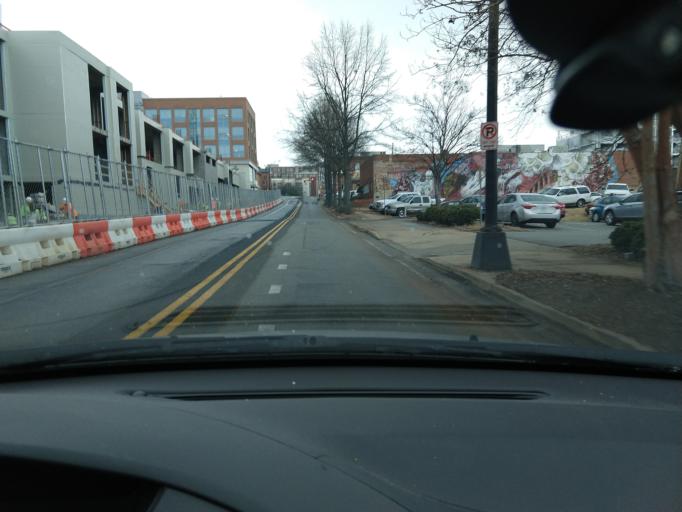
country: US
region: South Carolina
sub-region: Greenville County
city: Greenville
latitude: 34.8459
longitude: -82.3996
